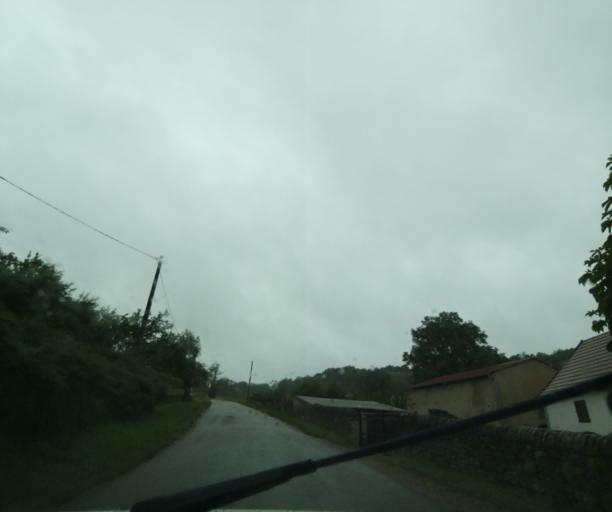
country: FR
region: Bourgogne
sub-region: Departement de Saone-et-Loire
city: Charolles
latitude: 46.4096
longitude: 4.2563
